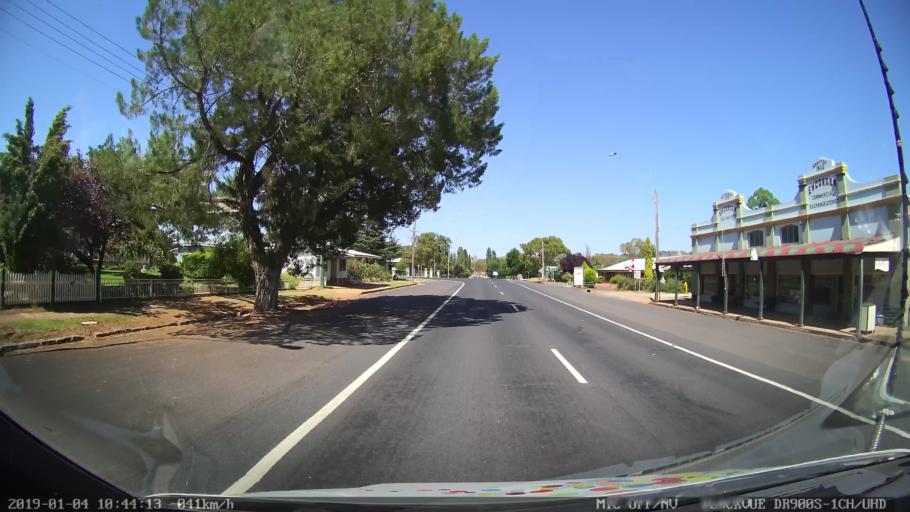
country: AU
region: New South Wales
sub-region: Cabonne
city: Molong
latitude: -33.2869
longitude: 148.7387
